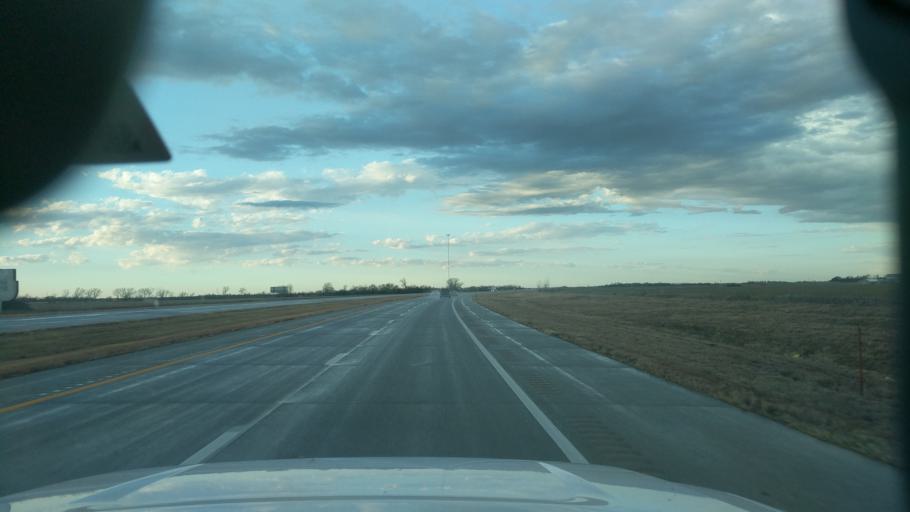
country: US
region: Kansas
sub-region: Harvey County
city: Hesston
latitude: 38.1545
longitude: -97.4289
